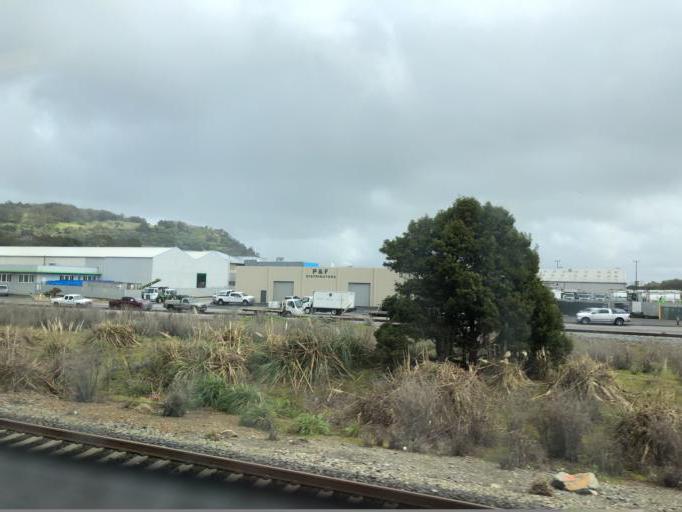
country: US
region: California
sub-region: San Mateo County
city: Brisbane
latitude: 37.7058
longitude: -122.4019
